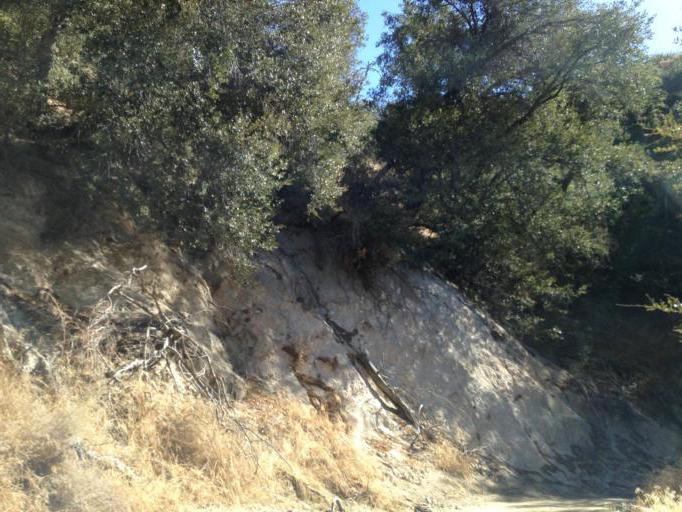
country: US
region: California
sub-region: San Bernardino County
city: Running Springs
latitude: 34.1638
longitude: -117.0967
